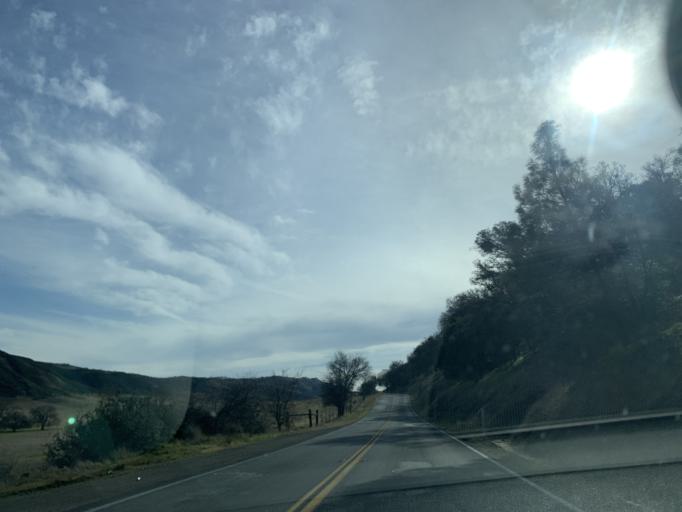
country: US
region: California
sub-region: Monterey County
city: Greenfield
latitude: 36.4947
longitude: -121.0820
